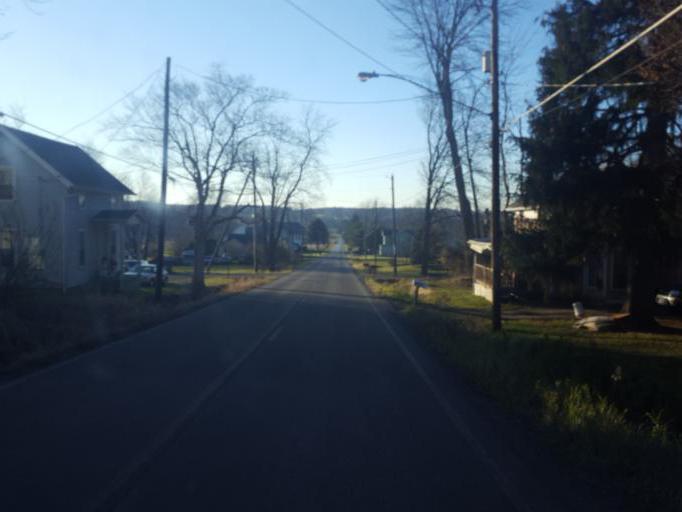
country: US
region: Ohio
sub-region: Wayne County
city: Shreve
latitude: 40.8087
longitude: -82.1067
